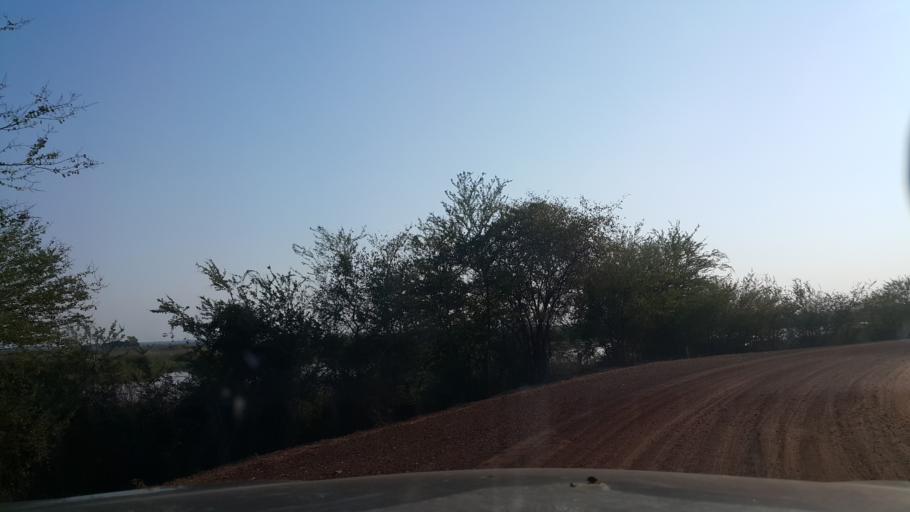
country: TH
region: Changwat Udon Thani
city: Ban Na Muang
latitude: 17.2249
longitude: 103.0489
